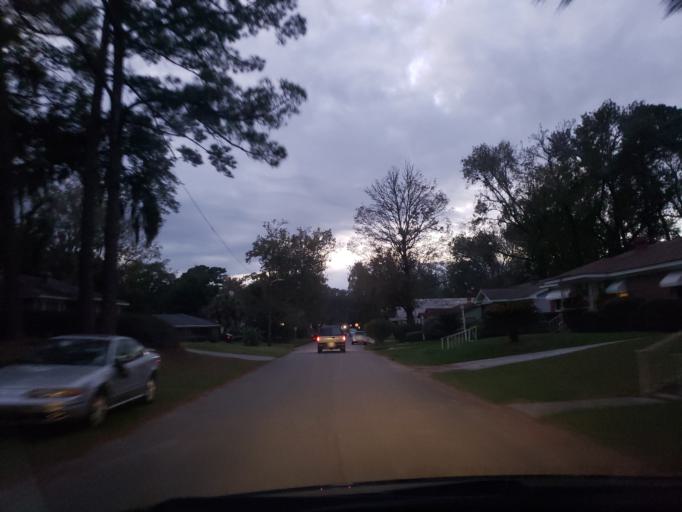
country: US
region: Georgia
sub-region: Chatham County
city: Thunderbolt
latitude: 32.0478
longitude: -81.0777
